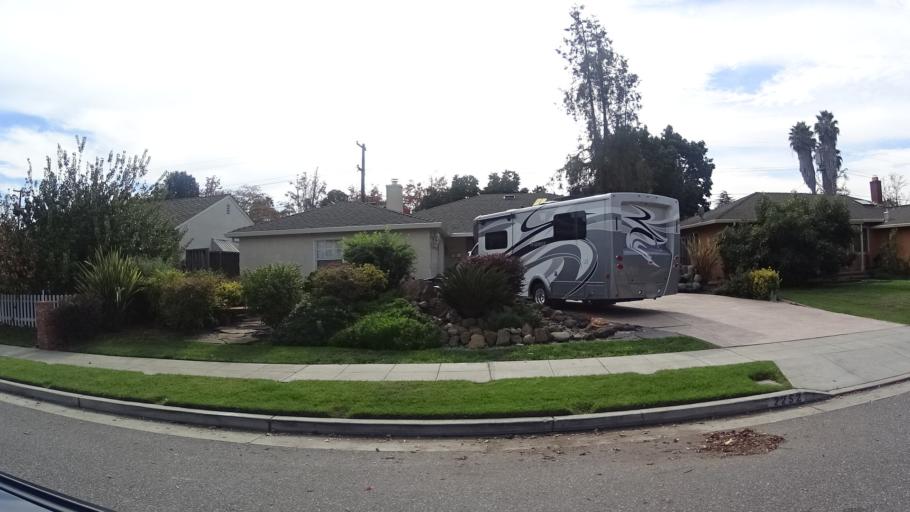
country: US
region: California
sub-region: Santa Clara County
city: Burbank
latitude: 37.3370
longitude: -121.9424
